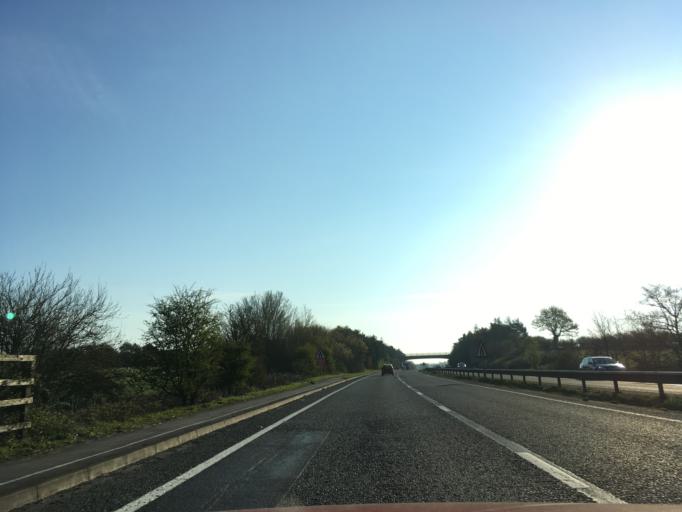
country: GB
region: England
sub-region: Oxfordshire
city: North Leigh
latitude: 51.7874
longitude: -1.4446
